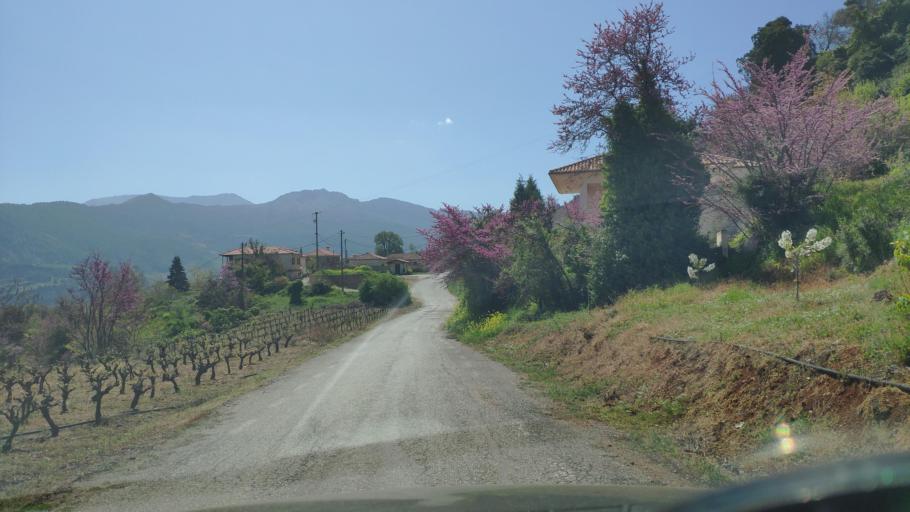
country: GR
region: West Greece
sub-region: Nomos Achaias
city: Akrata
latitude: 38.1004
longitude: 22.3181
